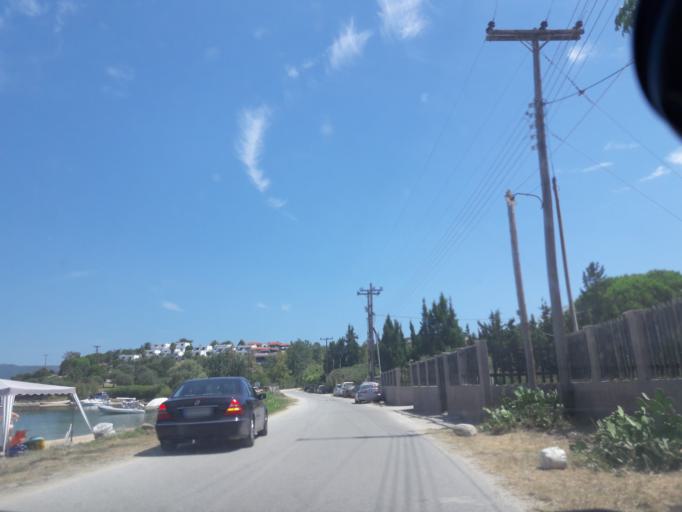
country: GR
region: Central Macedonia
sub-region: Nomos Chalkidikis
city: Ouranoupolis
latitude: 40.3169
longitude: 23.9255
